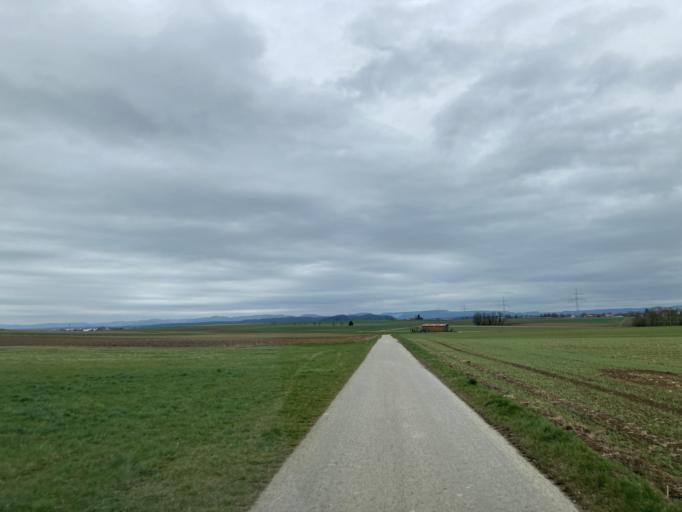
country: DE
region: Baden-Wuerttemberg
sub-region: Regierungsbezirk Stuttgart
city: Bondorf
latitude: 48.4826
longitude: 8.8537
